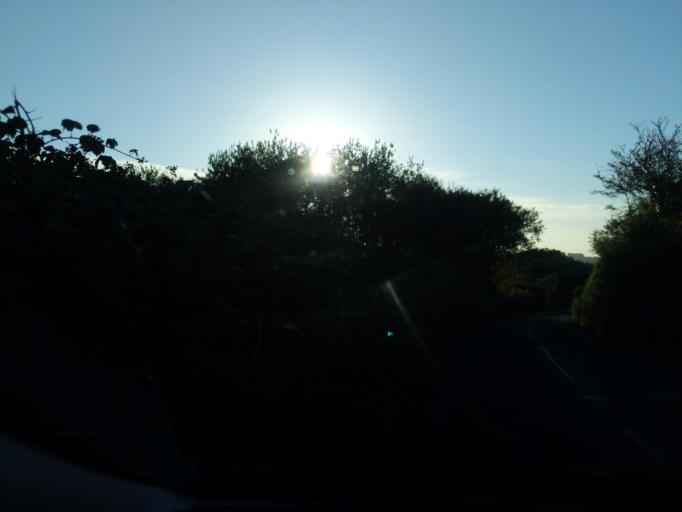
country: GB
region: England
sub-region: Plymouth
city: Plymstock
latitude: 50.3453
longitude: -4.1184
